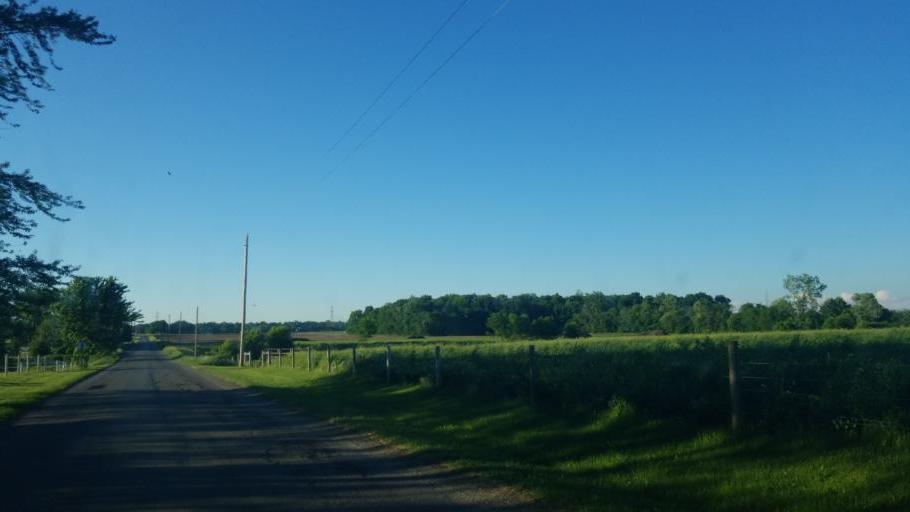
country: US
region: Indiana
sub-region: Elkhart County
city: Nappanee
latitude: 41.4192
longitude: -86.0588
